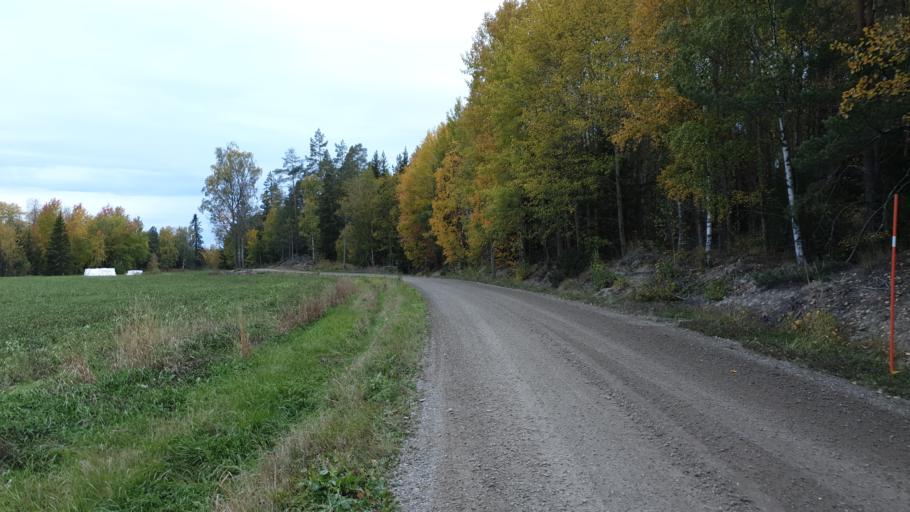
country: SE
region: Vaestmanland
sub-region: Sala Kommun
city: Sala
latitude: 59.8189
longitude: 16.6501
